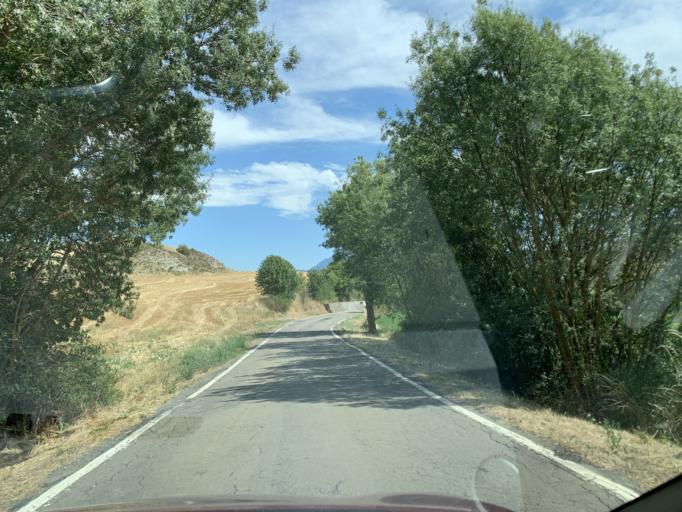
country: ES
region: Aragon
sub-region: Provincia de Huesca
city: Santa Cruz de la Seros
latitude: 42.5948
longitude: -0.6447
